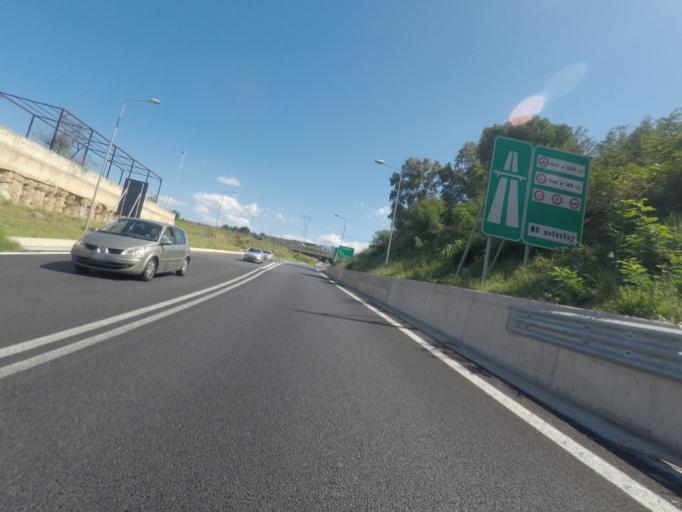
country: IT
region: Calabria
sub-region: Provincia di Reggio Calabria
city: Campo Calabro
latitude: 38.2048
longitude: 15.6375
